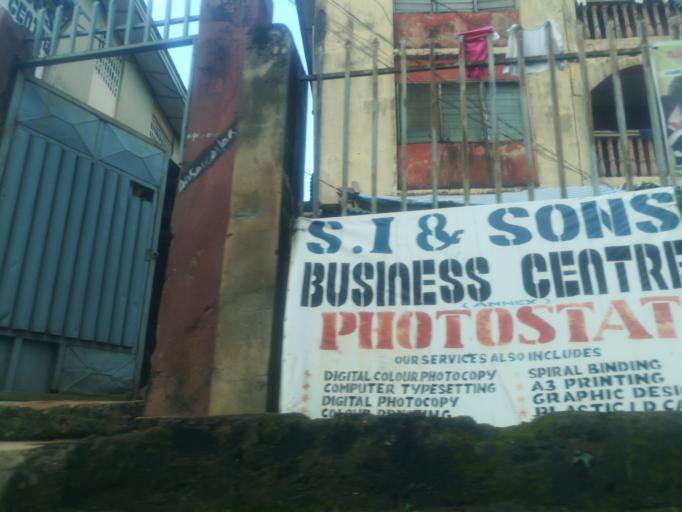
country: NG
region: Oyo
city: Ibadan
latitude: 7.4062
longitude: 3.9459
